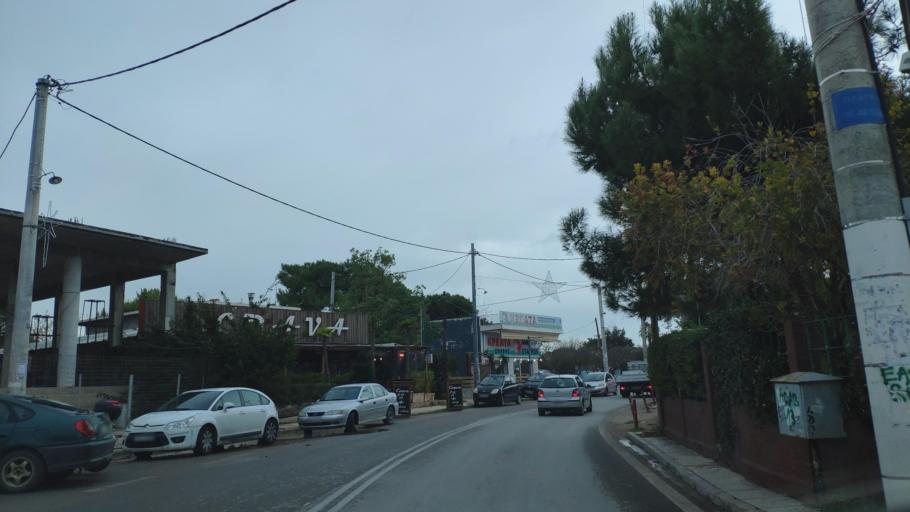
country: GR
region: Attica
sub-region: Nomarchia Anatolikis Attikis
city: Artemida
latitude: 37.9779
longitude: 24.0082
